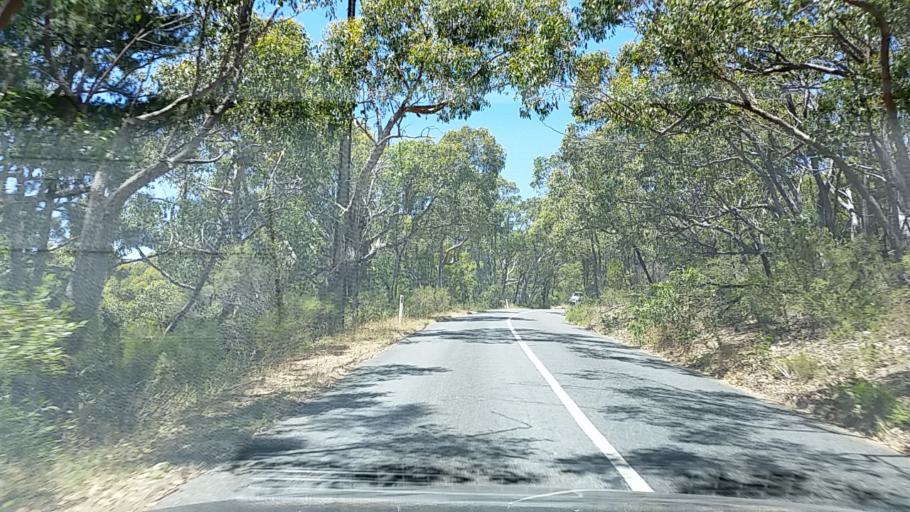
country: AU
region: South Australia
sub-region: Adelaide Hills
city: Crafers
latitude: -34.9891
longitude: 138.6849
